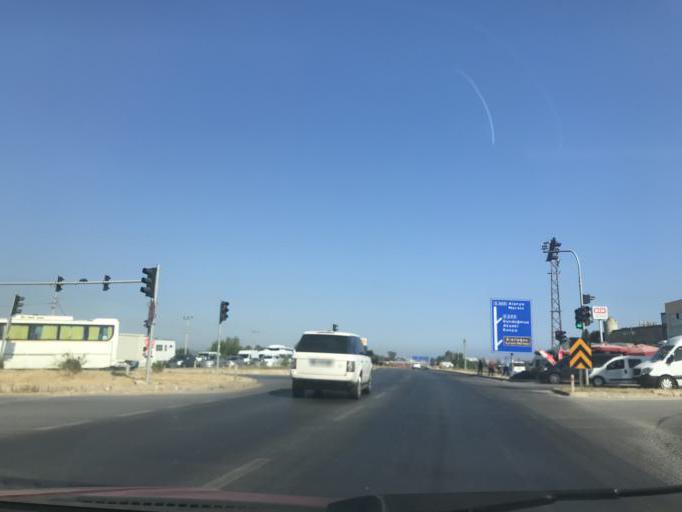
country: TR
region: Antalya
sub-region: Manavgat
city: Kizilagac
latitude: 36.7308
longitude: 31.5438
